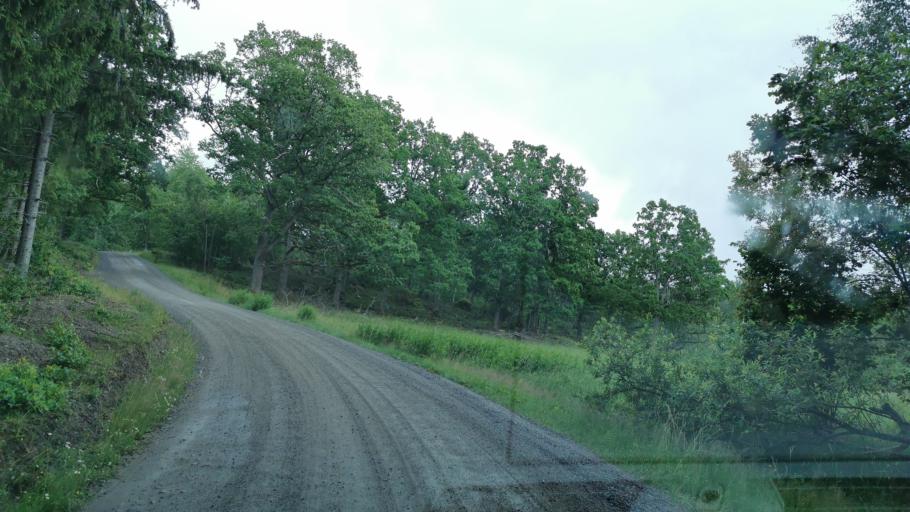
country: SE
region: OEstergoetland
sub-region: Atvidabergs Kommun
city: Atvidaberg
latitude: 58.1841
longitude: 16.1263
